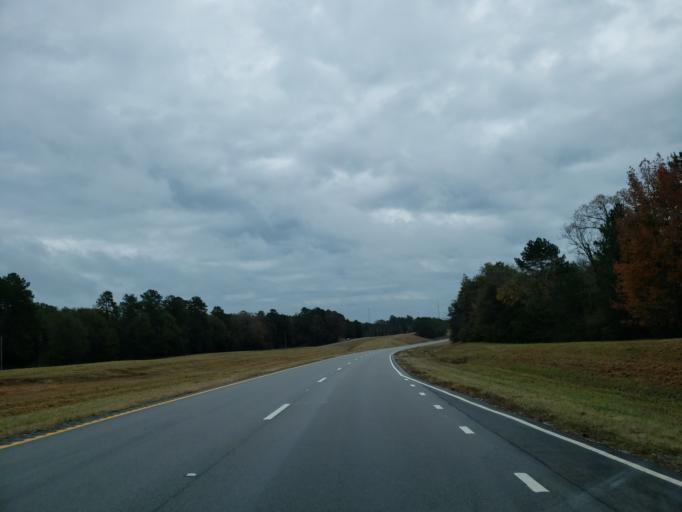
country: US
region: Mississippi
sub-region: Wayne County
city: Waynesboro
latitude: 31.6958
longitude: -88.7228
